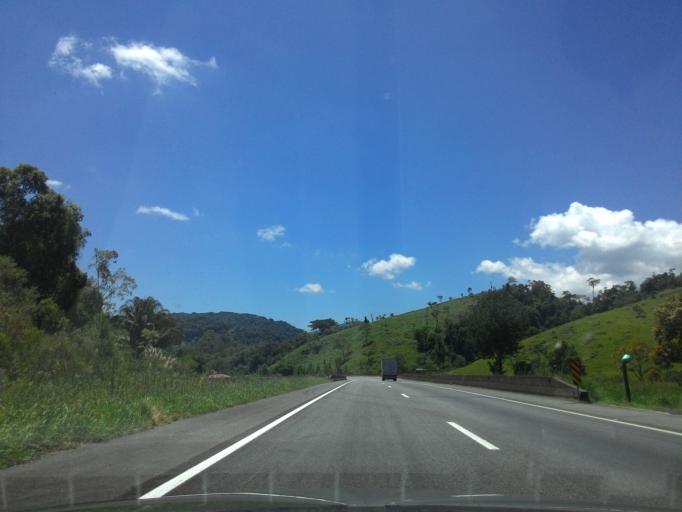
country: BR
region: Parana
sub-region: Antonina
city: Antonina
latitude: -25.0414
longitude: -48.5387
